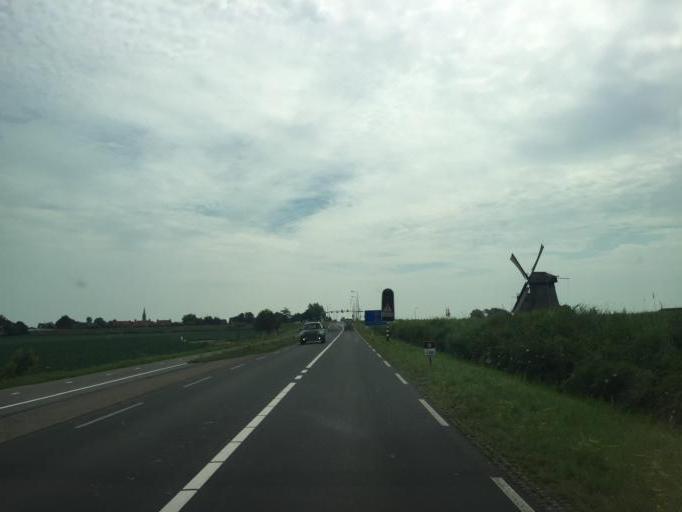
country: NL
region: North Holland
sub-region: Gemeente Heerhugowaard
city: Heerhugowaard
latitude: 52.6013
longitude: 4.8711
